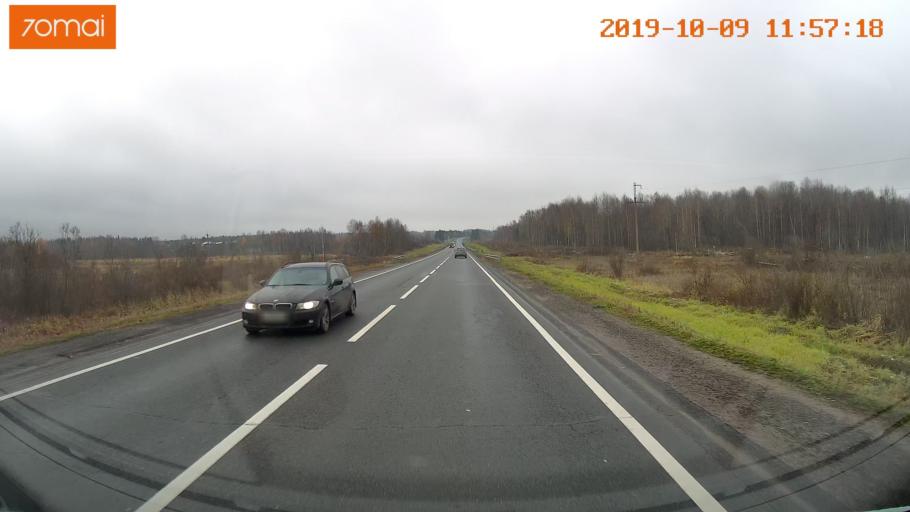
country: RU
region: Vologda
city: Gryazovets
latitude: 58.7341
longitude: 40.2918
